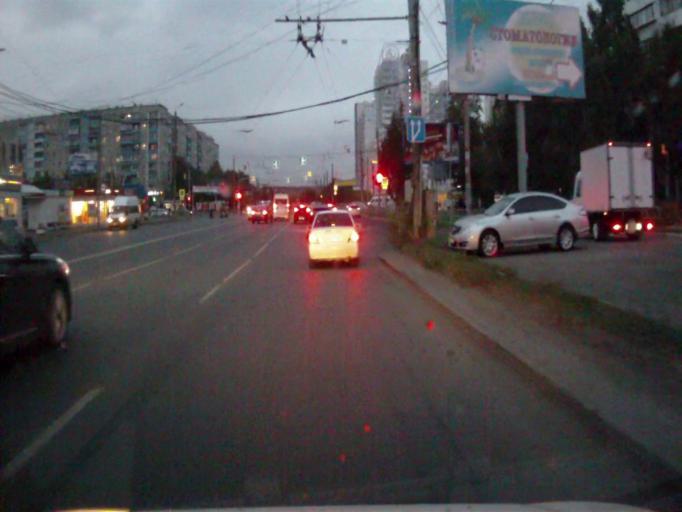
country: RU
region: Chelyabinsk
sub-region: Gorod Chelyabinsk
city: Chelyabinsk
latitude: 55.1798
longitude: 61.3326
